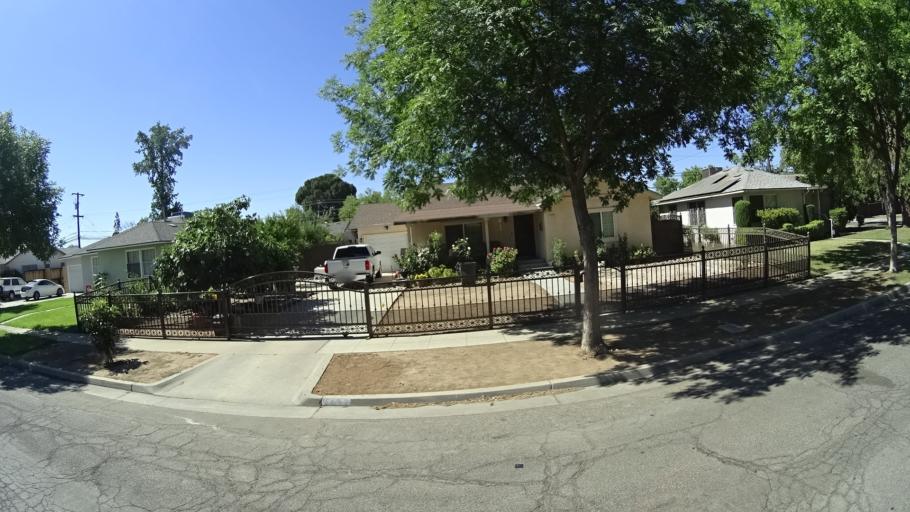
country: US
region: California
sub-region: Fresno County
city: Fresno
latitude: 36.7873
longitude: -119.8304
